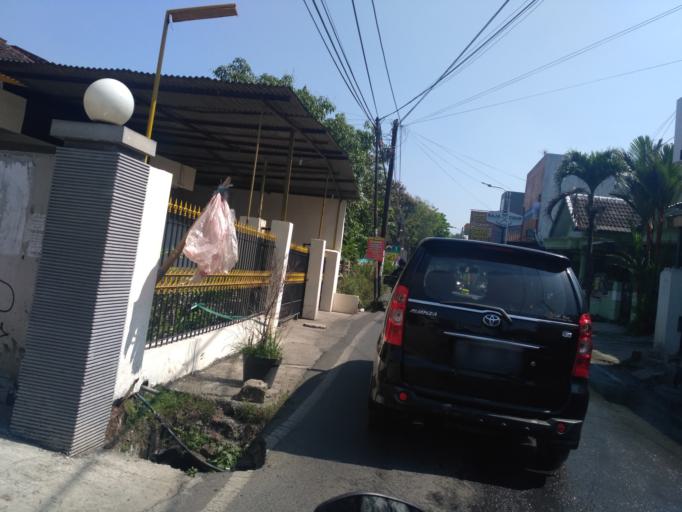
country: ID
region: East Java
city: Malang
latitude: -7.9340
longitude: 112.6145
